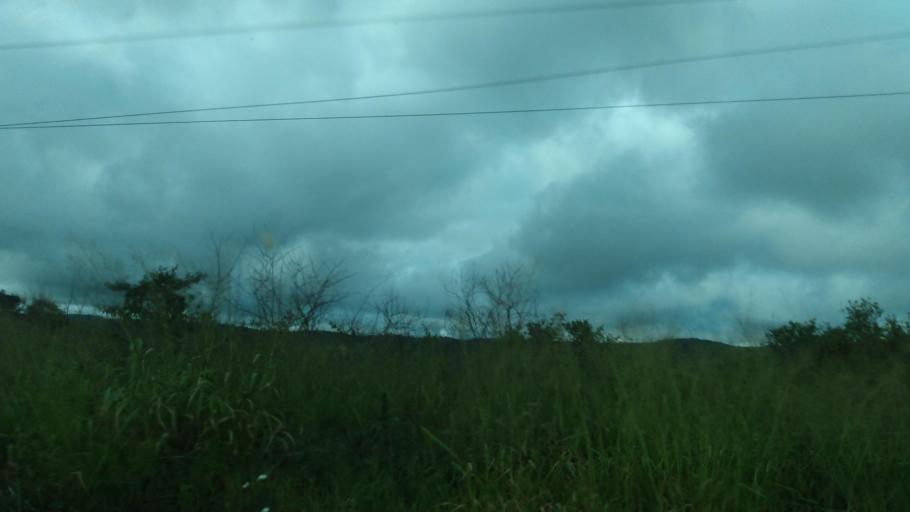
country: BR
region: Pernambuco
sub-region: Caruaru
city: Caruaru
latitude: -8.3169
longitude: -35.9779
